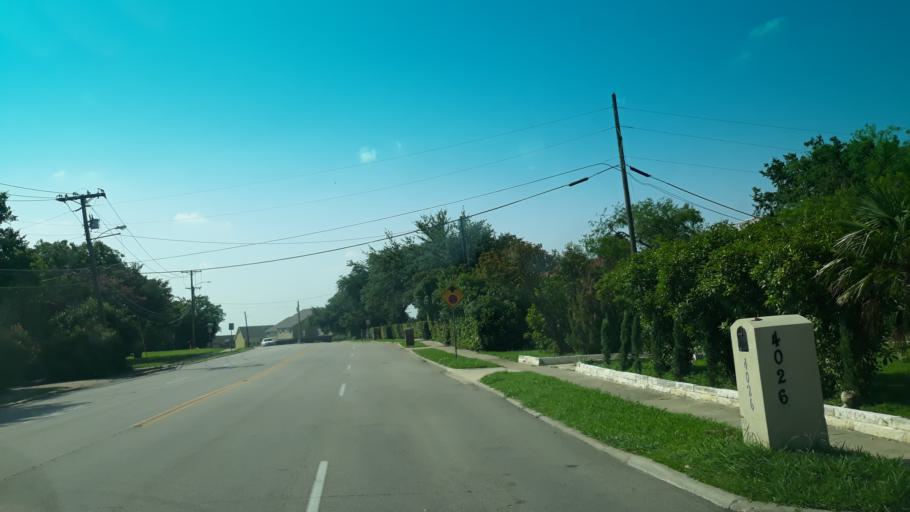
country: US
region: Texas
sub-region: Dallas County
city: Irving
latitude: 32.8578
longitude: -96.9804
